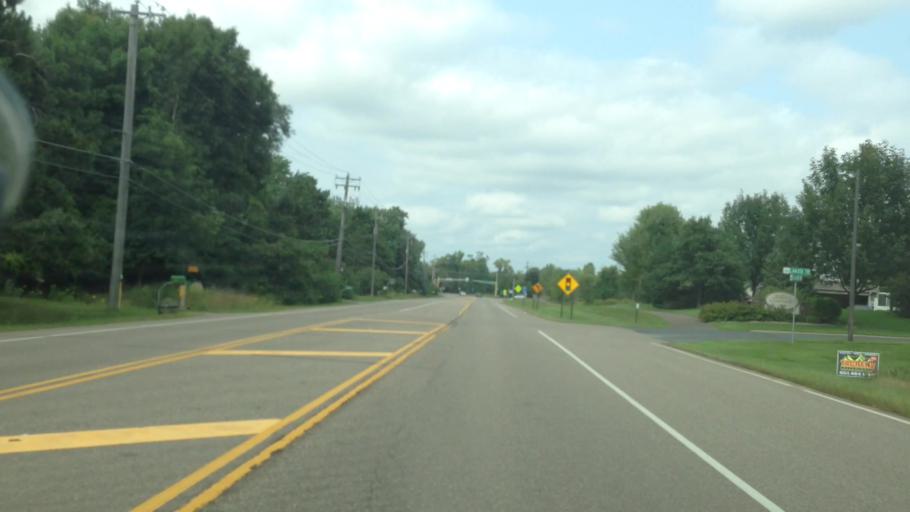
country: US
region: Minnesota
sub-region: Anoka County
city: Circle Pines
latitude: 45.1391
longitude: -93.1268
